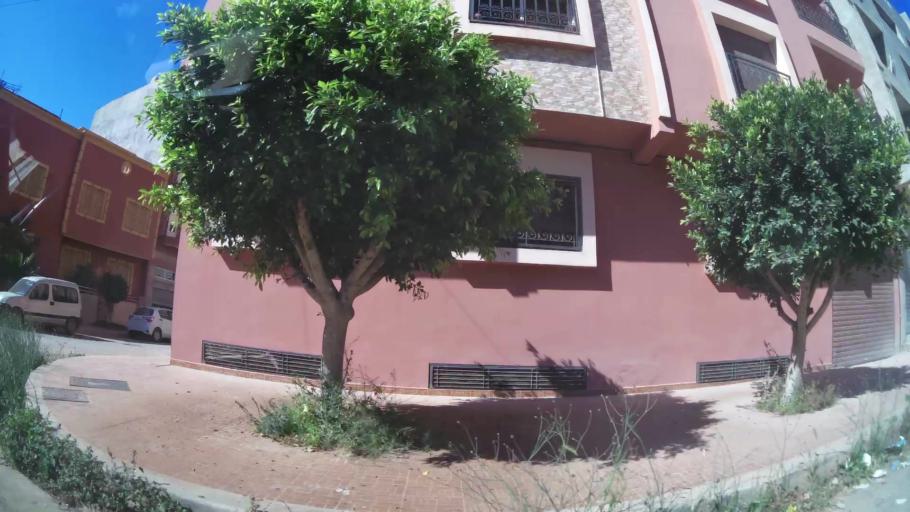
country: MA
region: Oriental
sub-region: Berkane-Taourirt
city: Berkane
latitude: 34.9405
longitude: -2.3321
